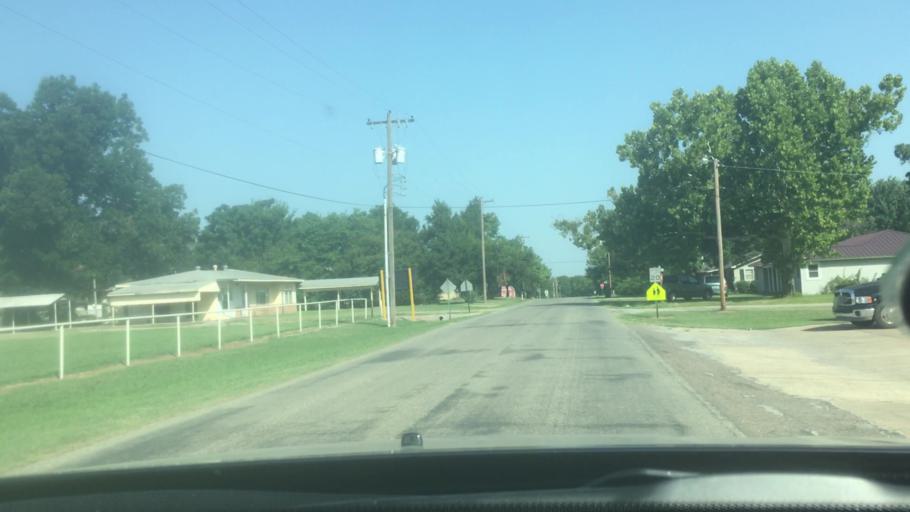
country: US
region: Oklahoma
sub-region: Bryan County
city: Calera
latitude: 33.9370
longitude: -96.4292
